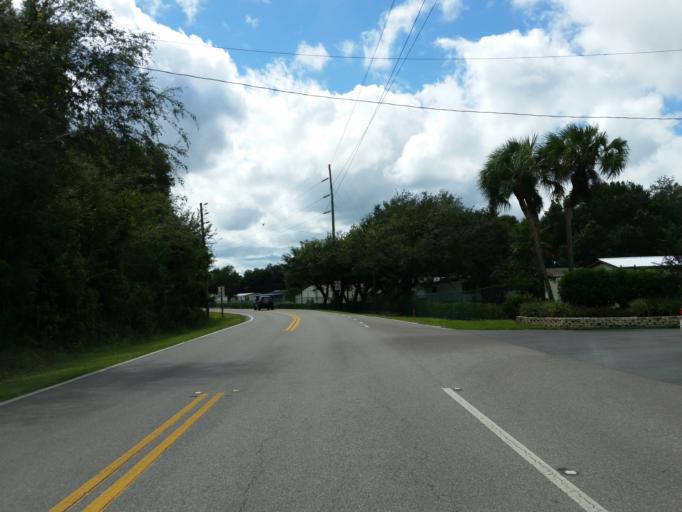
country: US
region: Florida
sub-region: Pasco County
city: Zephyrhills West
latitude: 28.2033
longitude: -82.2465
